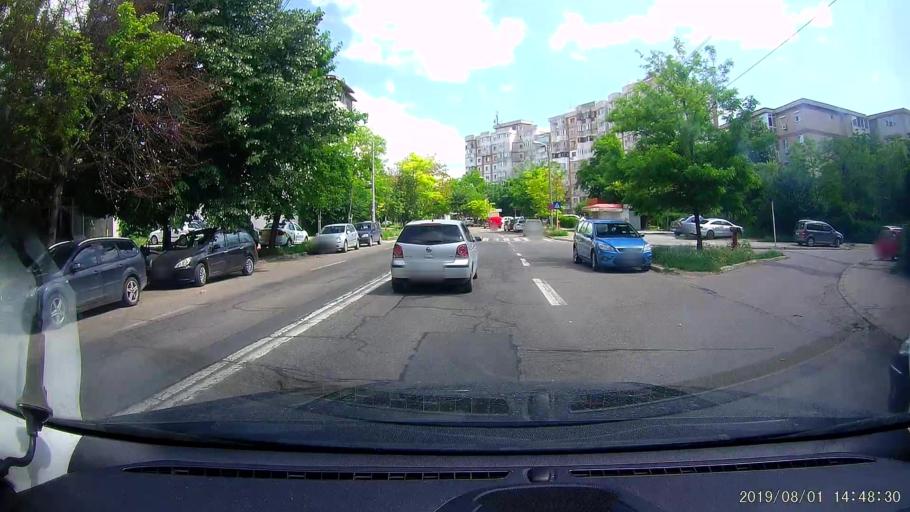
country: RO
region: Galati
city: Galati
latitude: 45.4101
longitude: 28.0095
